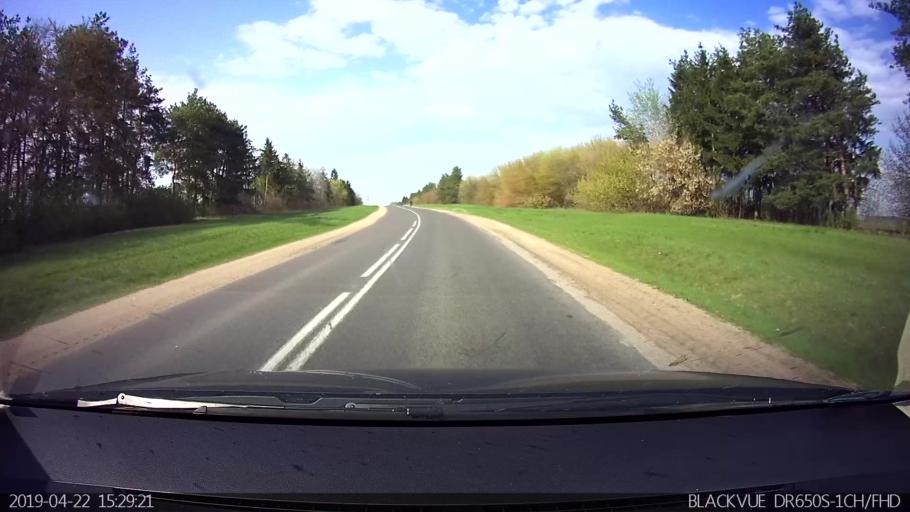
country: BY
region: Brest
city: Vysokaye
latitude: 52.3850
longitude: 23.3733
